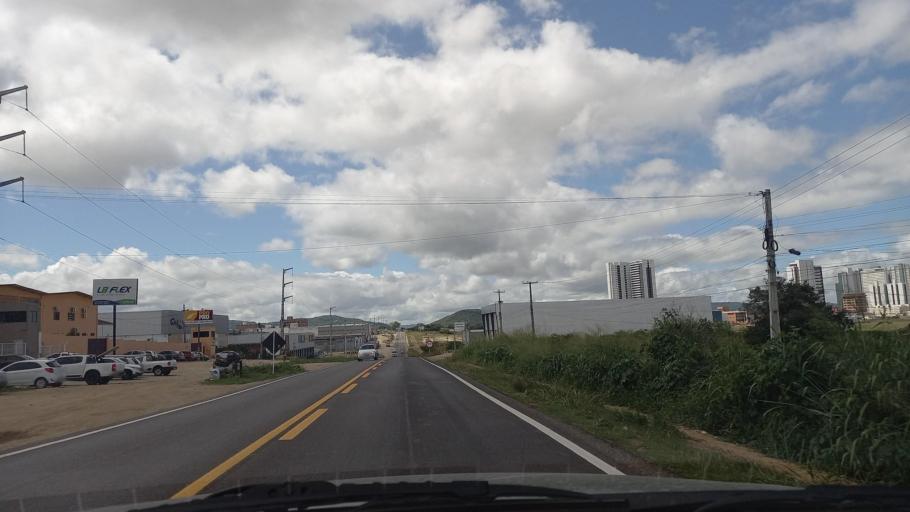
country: BR
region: Pernambuco
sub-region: Caruaru
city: Caruaru
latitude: -8.2531
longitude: -35.9729
